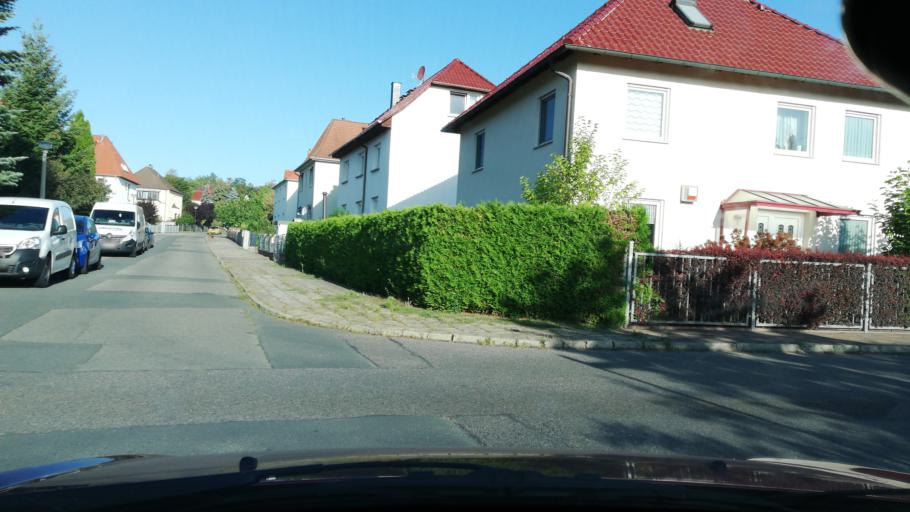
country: DE
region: Saxony-Anhalt
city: Halle Neustadt
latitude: 51.4912
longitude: 11.9091
